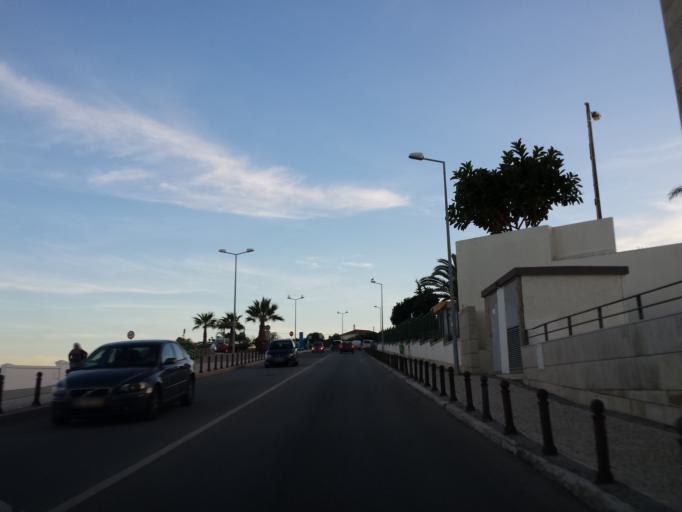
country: PT
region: Faro
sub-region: Lagos
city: Lagos
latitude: 37.0981
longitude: -8.6687
